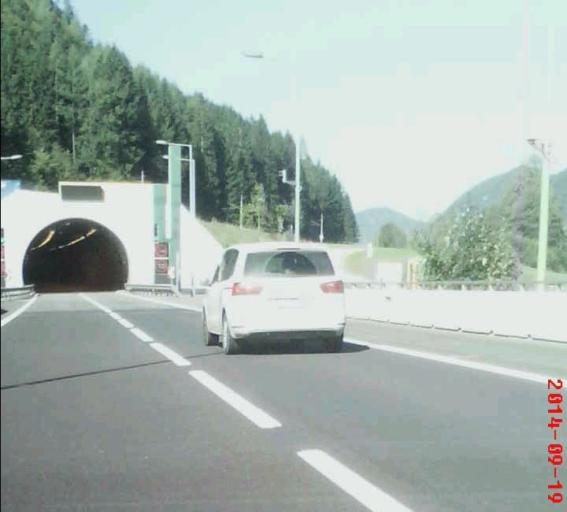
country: AT
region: Upper Austria
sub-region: Politischer Bezirk Kirchdorf an der Krems
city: Rossleithen
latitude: 47.7512
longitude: 14.2470
